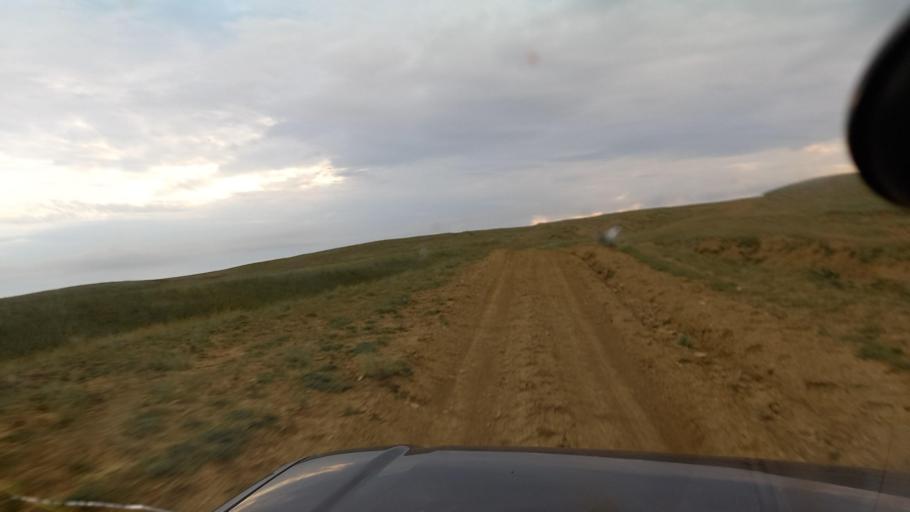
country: RU
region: Krasnodarskiy
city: Taman'
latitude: 45.2010
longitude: 36.7920
